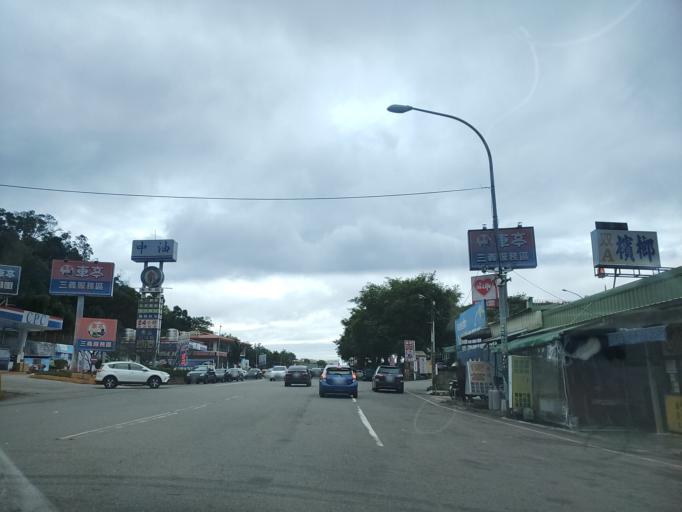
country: TW
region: Taiwan
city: Fengyuan
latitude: 24.3908
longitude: 120.7592
